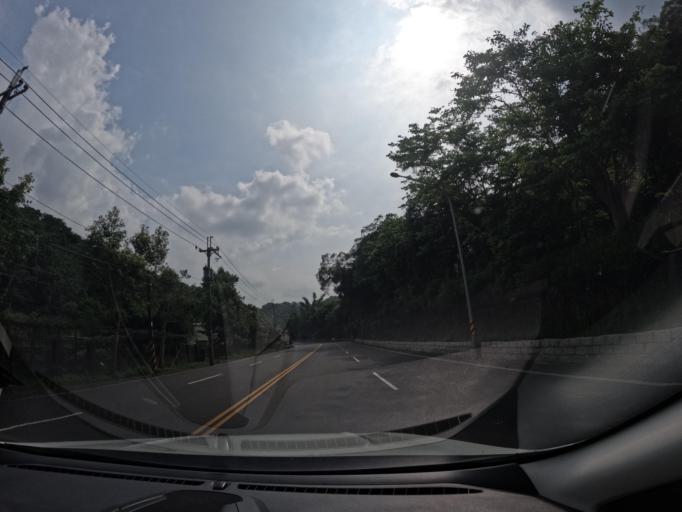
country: TW
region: Taiwan
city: Daxi
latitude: 24.8992
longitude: 121.3394
